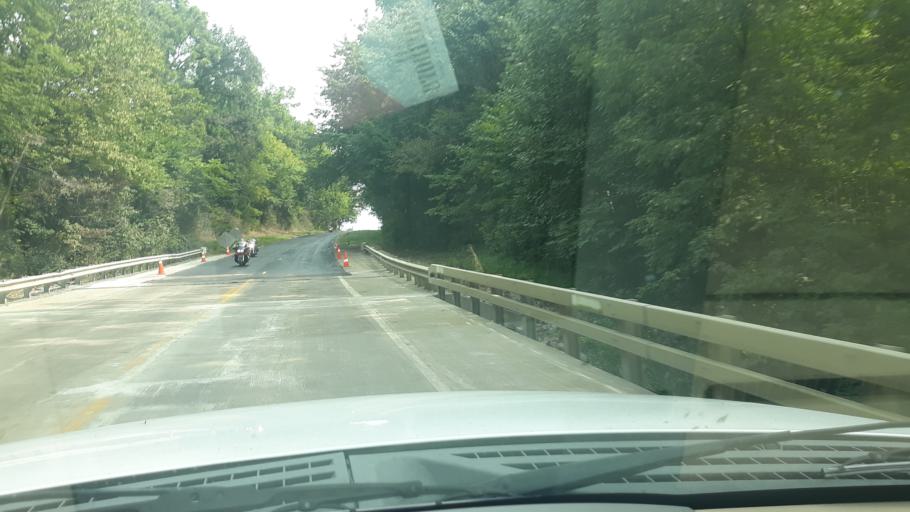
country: US
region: Illinois
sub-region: Edwards County
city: Grayville
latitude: 38.2862
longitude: -87.9799
